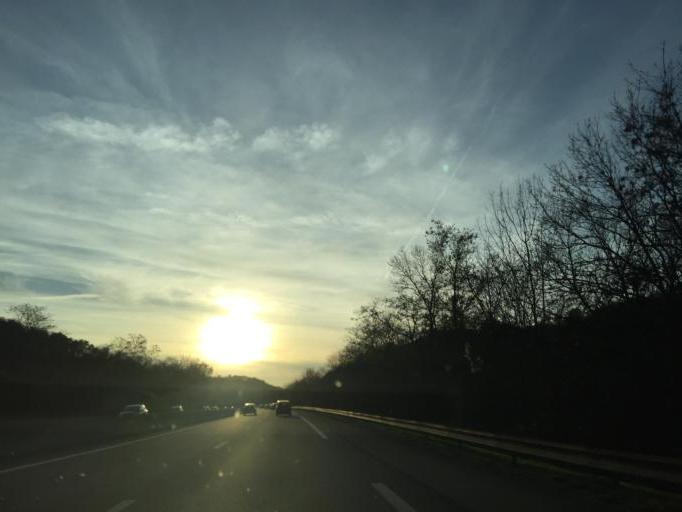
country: FR
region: Rhone-Alpes
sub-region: Departement du Rhone
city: Echalas
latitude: 45.5492
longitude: 4.6759
